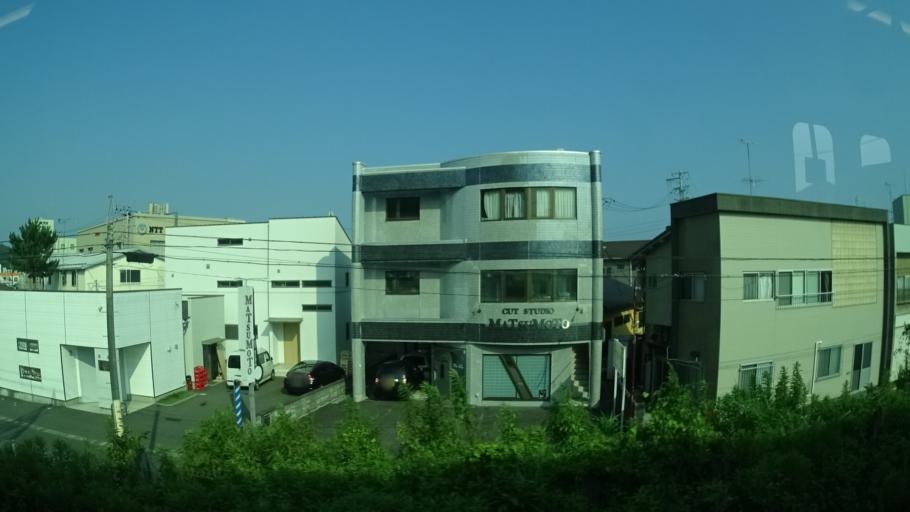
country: JP
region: Ibaraki
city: Kitaibaraki
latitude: 36.9181
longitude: 140.7961
